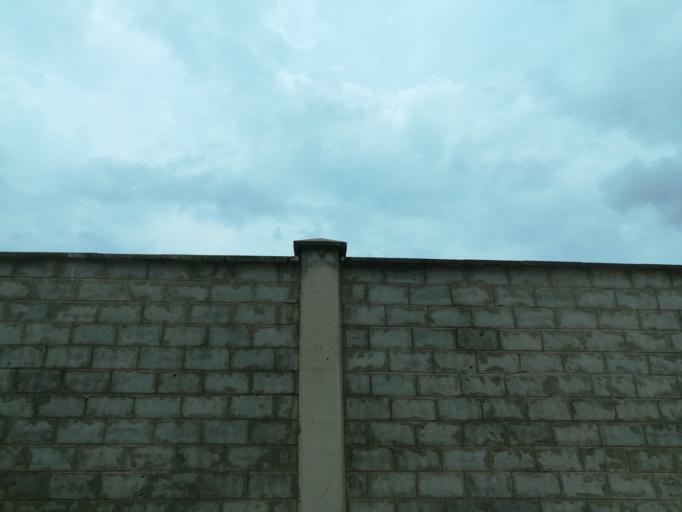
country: NG
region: Lagos
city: Oshodi
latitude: 6.5555
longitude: 3.3259
